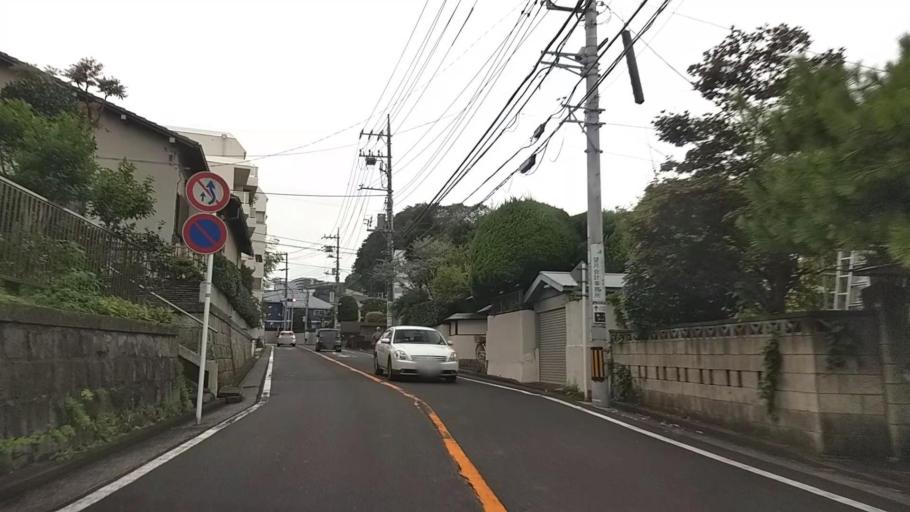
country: JP
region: Kanagawa
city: Yokohama
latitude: 35.4073
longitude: 139.6196
